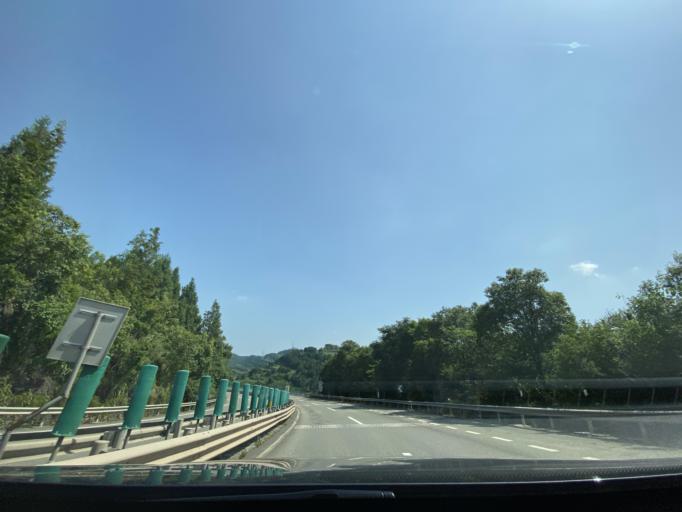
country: CN
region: Sichuan
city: Longquan
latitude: 30.5199
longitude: 104.3637
